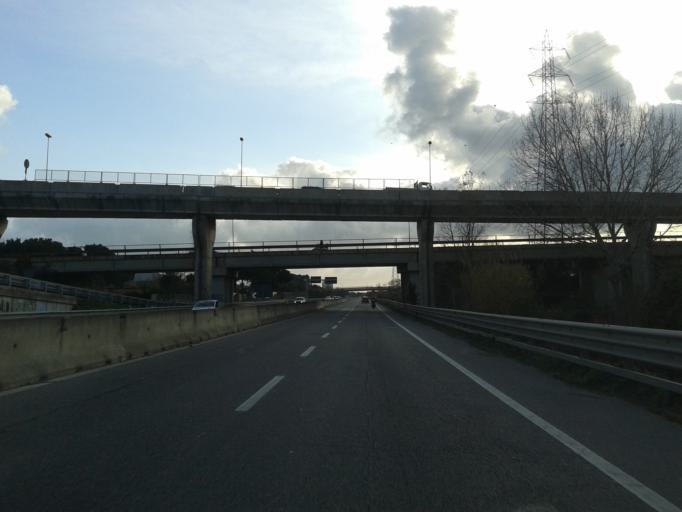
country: IT
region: Tuscany
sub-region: Provincia di Livorno
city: Livorno
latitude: 43.5323
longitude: 10.3336
